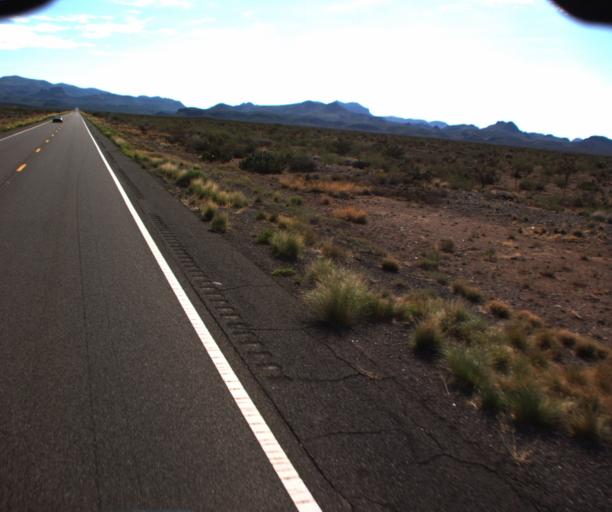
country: US
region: Arizona
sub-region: Graham County
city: Safford
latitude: 32.8230
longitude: -109.4703
